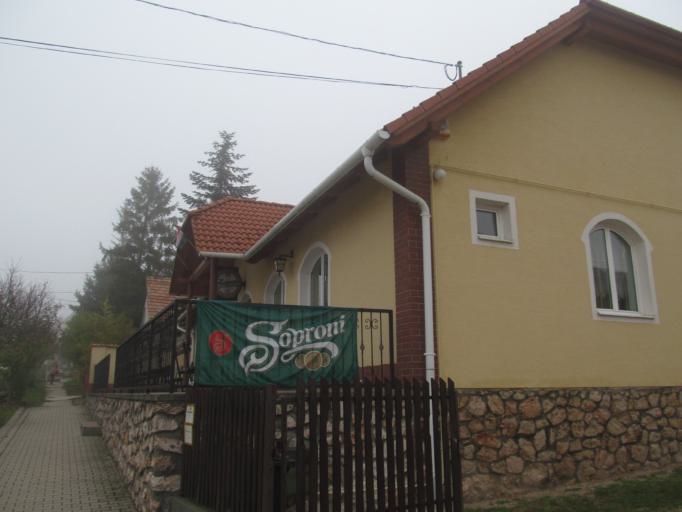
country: HU
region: Fejer
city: Bodajk
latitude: 47.3502
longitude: 18.2693
